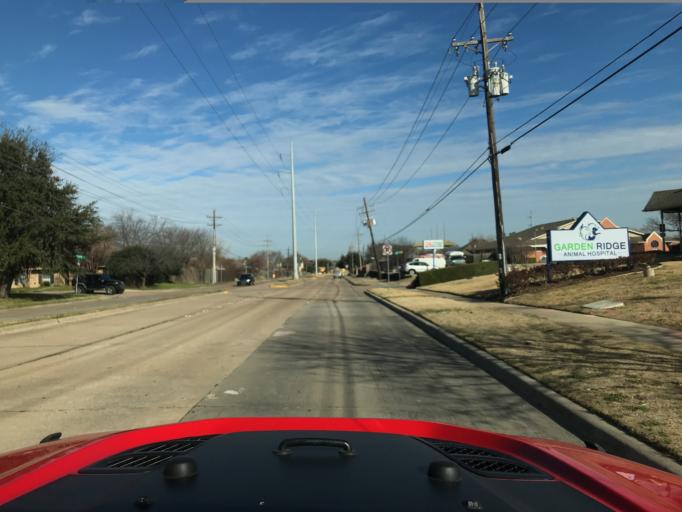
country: US
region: Texas
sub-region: Denton County
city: Lewisville
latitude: 33.0451
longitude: -97.0359
